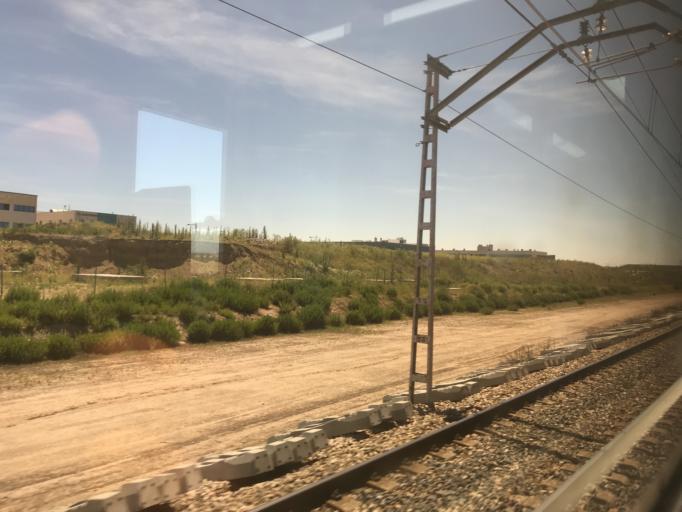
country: ES
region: Madrid
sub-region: Provincia de Madrid
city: Getafe
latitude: 40.2938
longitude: -3.7058
